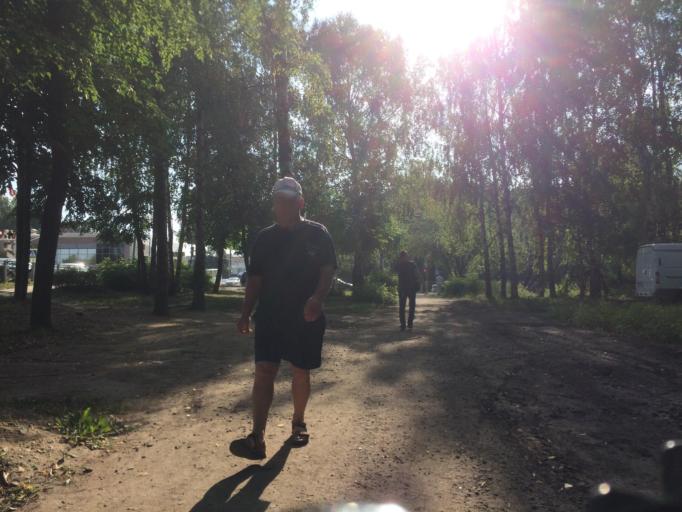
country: RU
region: Mariy-El
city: Medvedevo
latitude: 56.6406
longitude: 47.8441
